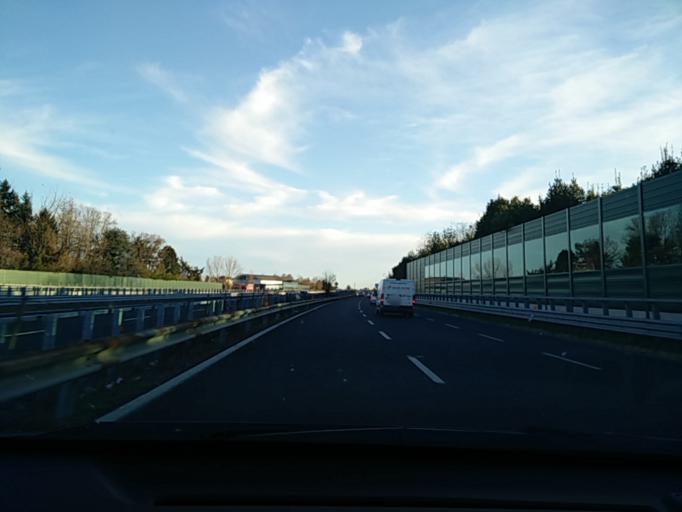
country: IT
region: Friuli Venezia Giulia
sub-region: Provincia di Udine
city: Passons
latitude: 46.0732
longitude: 13.1965
